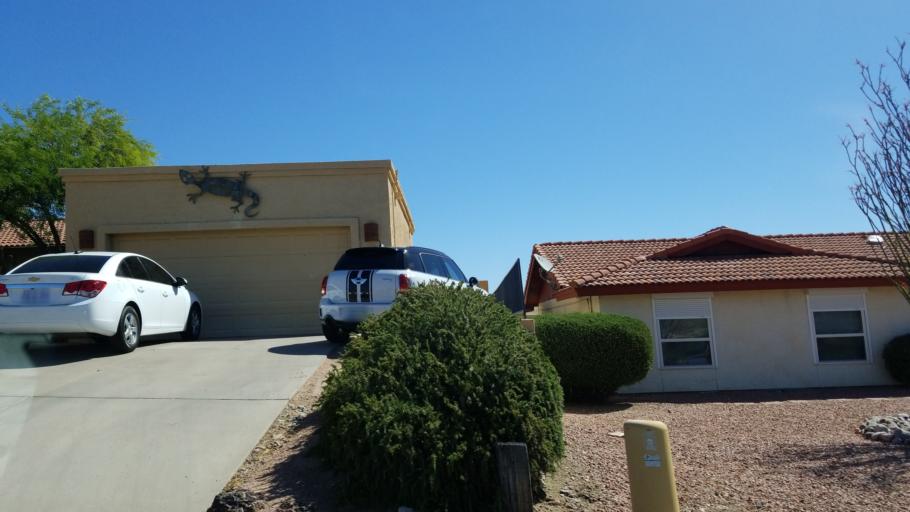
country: US
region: Arizona
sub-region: Maricopa County
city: Fountain Hills
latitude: 33.6123
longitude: -111.7305
